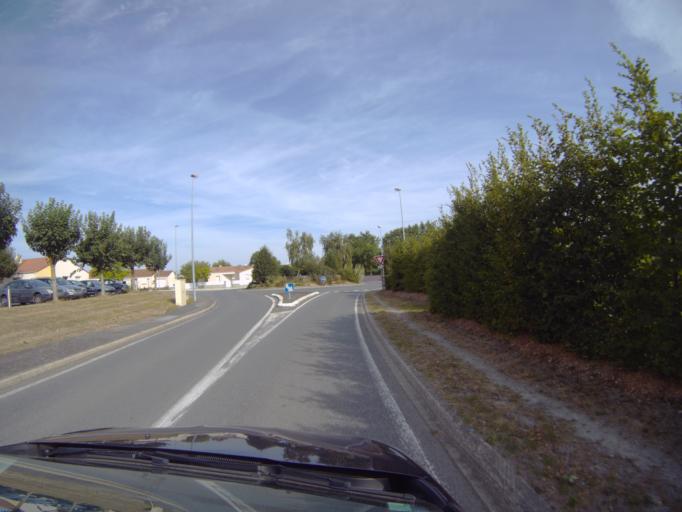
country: FR
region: Pays de la Loire
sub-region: Departement de la Vendee
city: Saint-Andre-Treize-Voies
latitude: 46.9116
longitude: -1.3806
